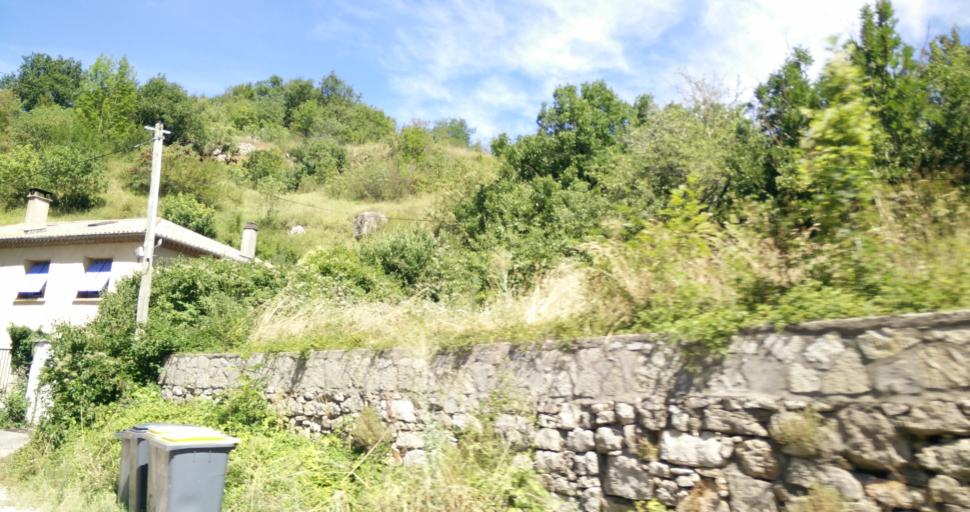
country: FR
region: Languedoc-Roussillon
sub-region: Departement du Gard
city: Aveze
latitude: 43.9711
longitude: 3.5718
